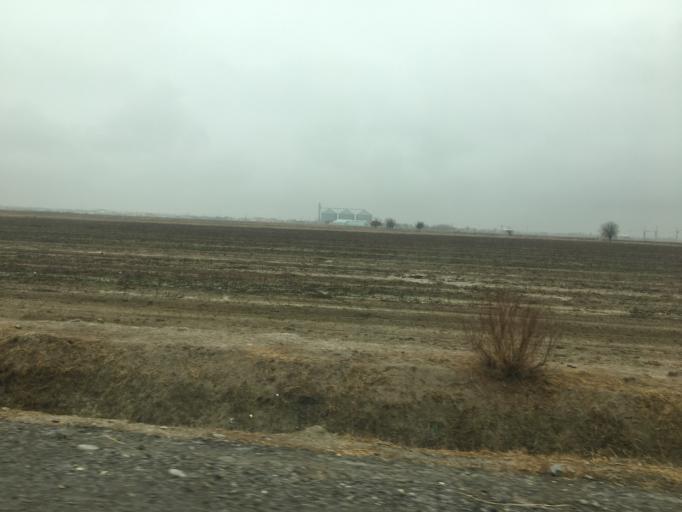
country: TM
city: Murgab
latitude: 37.4151
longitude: 62.1562
